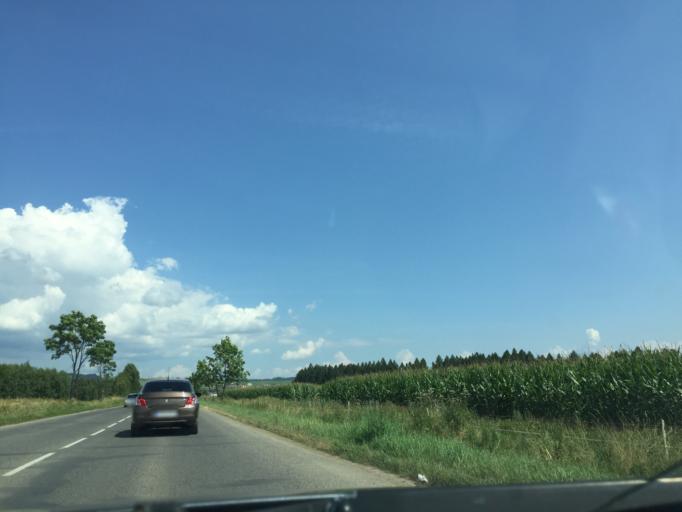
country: SK
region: Zilinsky
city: Namestovo
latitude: 49.4262
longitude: 19.4989
